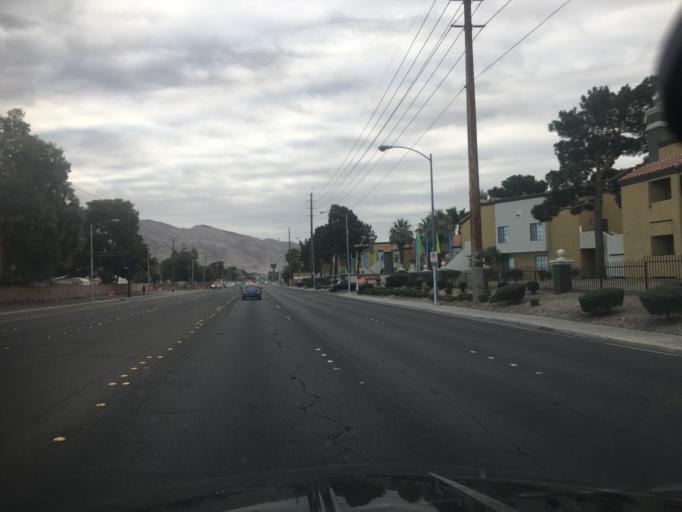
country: US
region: Nevada
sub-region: Clark County
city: Sunrise Manor
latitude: 36.1591
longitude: -115.0596
